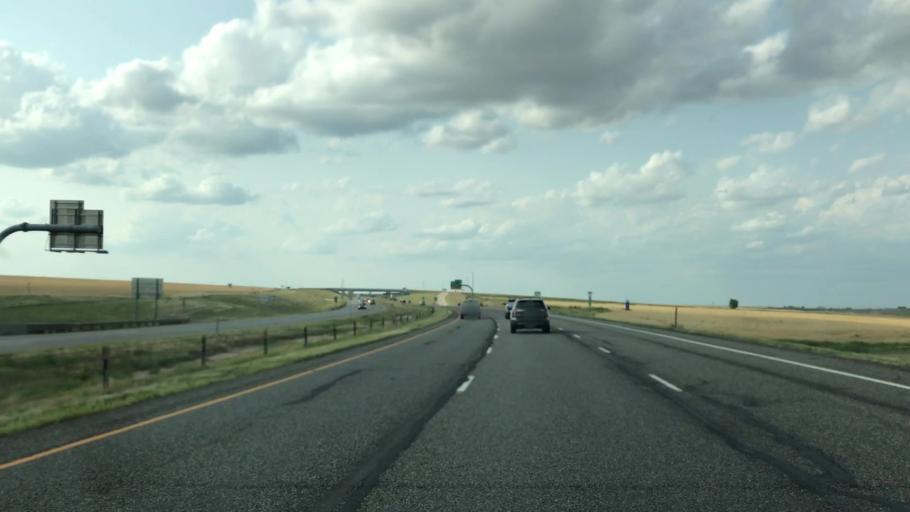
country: US
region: Colorado
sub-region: Adams County
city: Aurora
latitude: 39.8050
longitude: -104.7165
